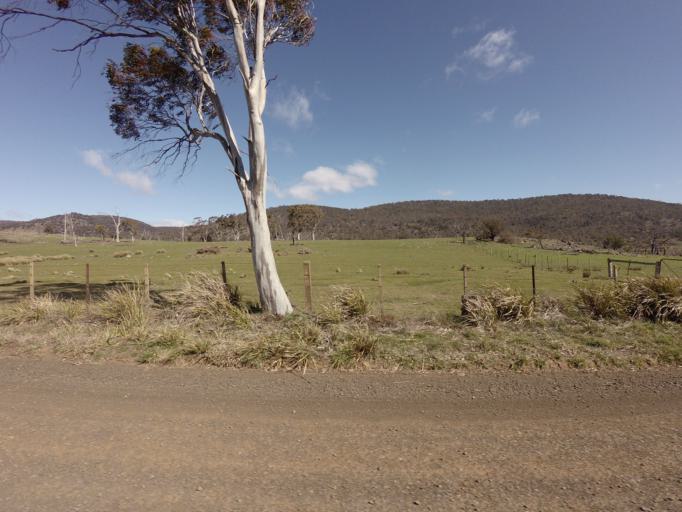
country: AU
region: Tasmania
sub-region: Northern Midlands
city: Evandale
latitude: -41.9400
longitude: 147.4237
